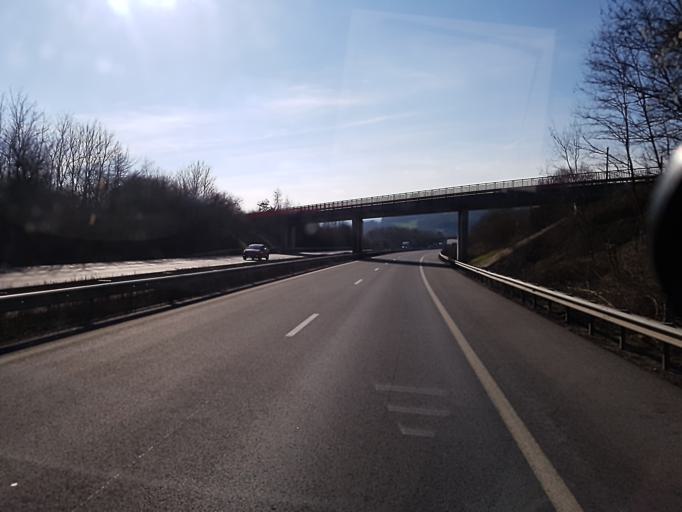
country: LU
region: Grevenmacher
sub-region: Canton de Grevenmacher
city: Mertert
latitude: 49.7091
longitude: 6.4809
